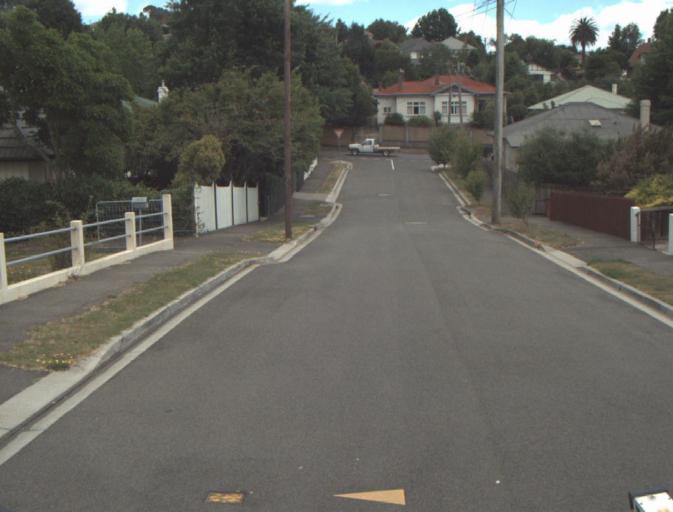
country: AU
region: Tasmania
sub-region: Launceston
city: East Launceston
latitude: -41.4432
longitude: 147.1593
